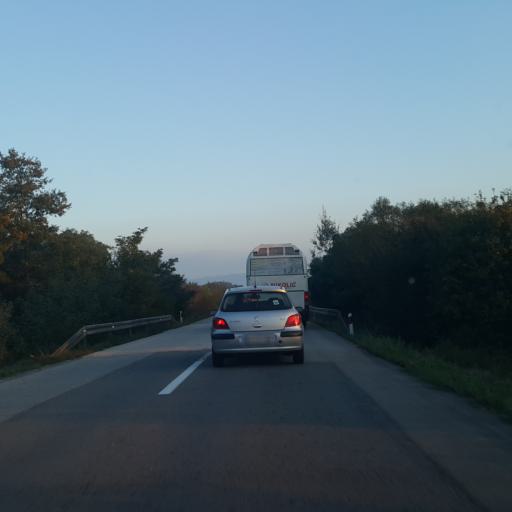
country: RS
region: Central Serbia
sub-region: Zajecarski Okrug
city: Zajecar
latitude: 43.9689
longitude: 22.2938
